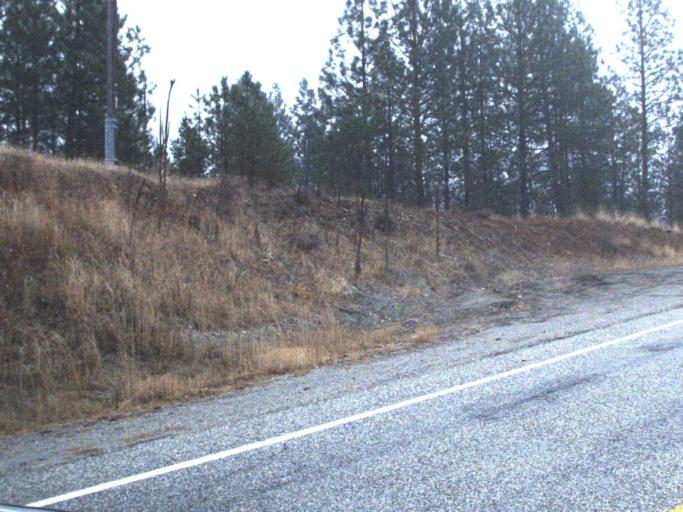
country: US
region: Washington
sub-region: Stevens County
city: Kettle Falls
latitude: 48.7320
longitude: -118.1302
